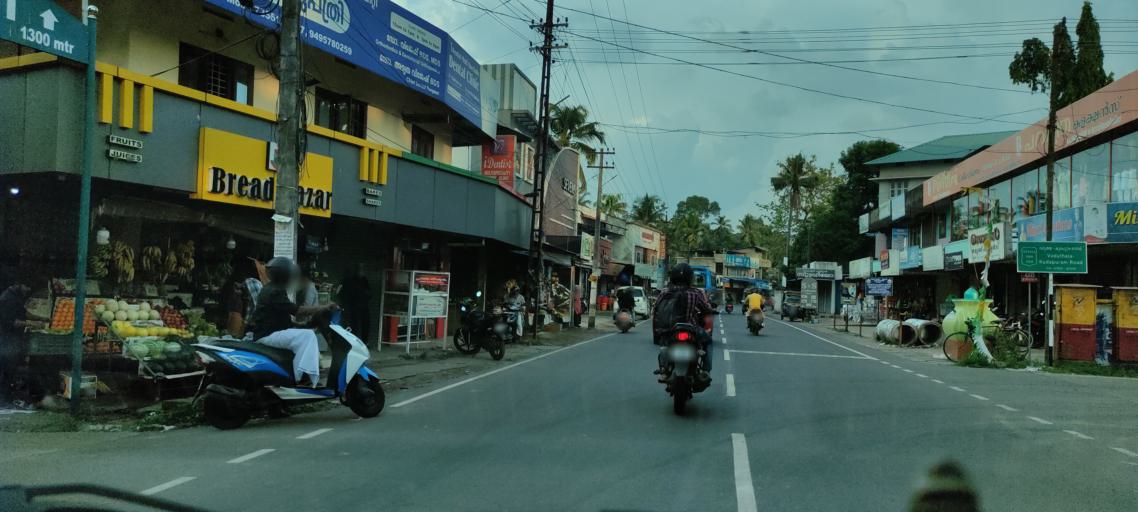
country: IN
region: Kerala
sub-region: Alappuzha
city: Arukutti
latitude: 9.8504
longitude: 76.3278
